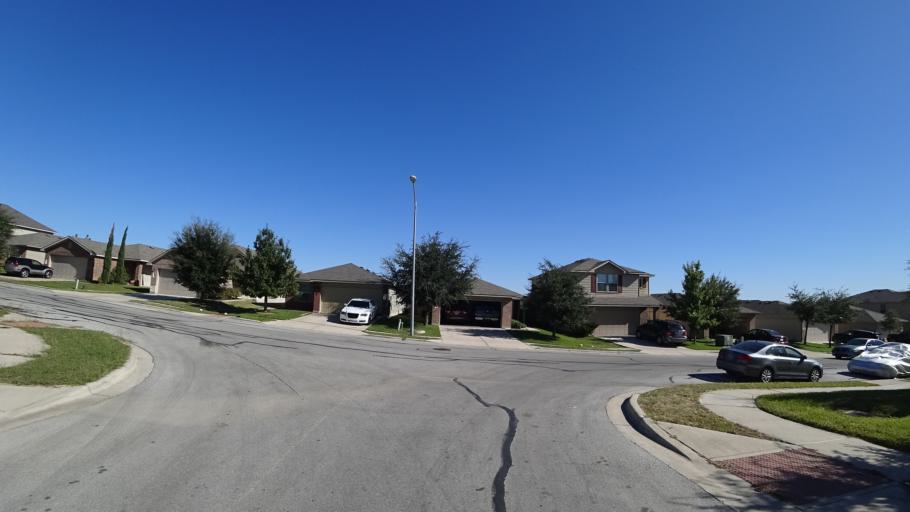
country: US
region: Texas
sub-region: Travis County
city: Hornsby Bend
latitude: 30.2795
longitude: -97.6278
